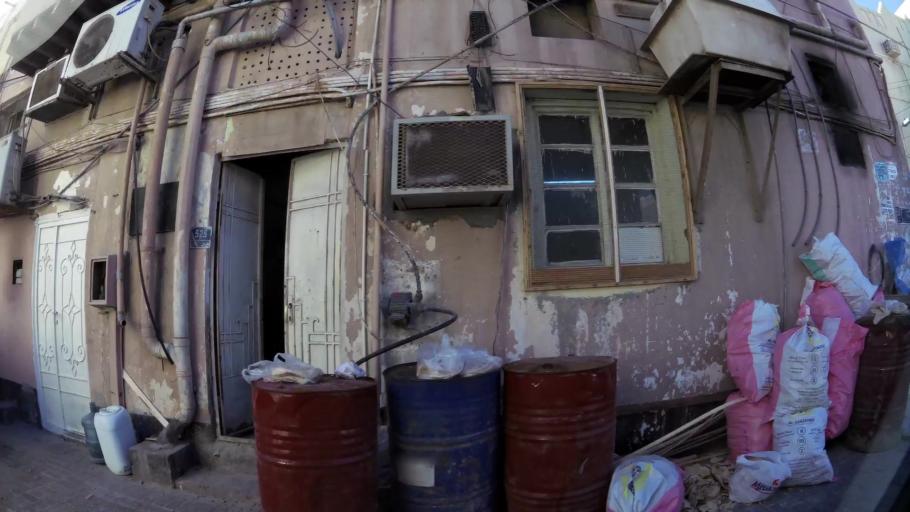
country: BH
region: Muharraq
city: Al Muharraq
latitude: 26.2591
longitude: 50.6131
